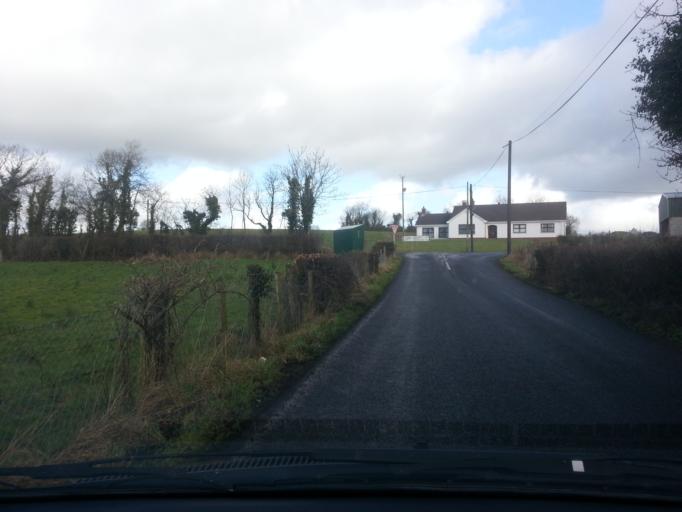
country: GB
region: Northern Ireland
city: Lisnaskea
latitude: 54.2779
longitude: -7.5103
